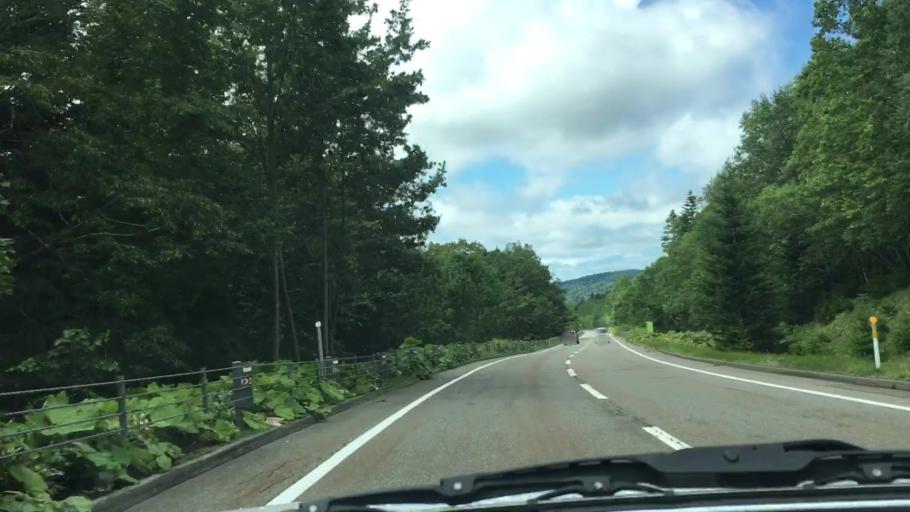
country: JP
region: Hokkaido
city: Kitami
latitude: 43.4099
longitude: 143.9639
